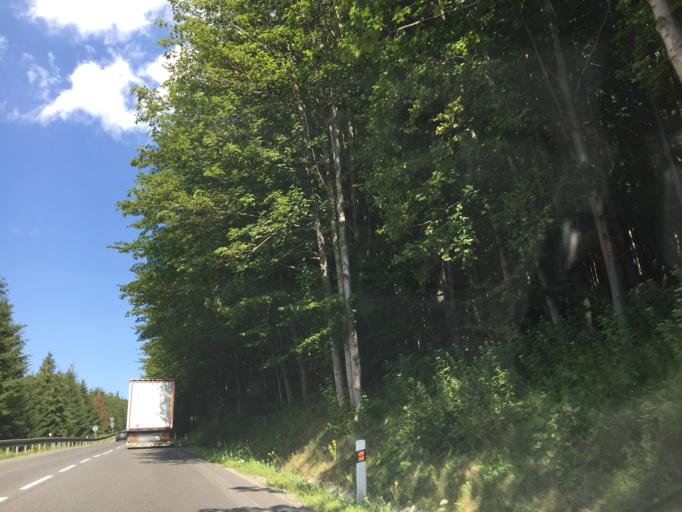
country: SK
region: Zilinsky
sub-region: Okres Dolny Kubin
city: Dolny Kubin
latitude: 49.2957
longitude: 19.3505
